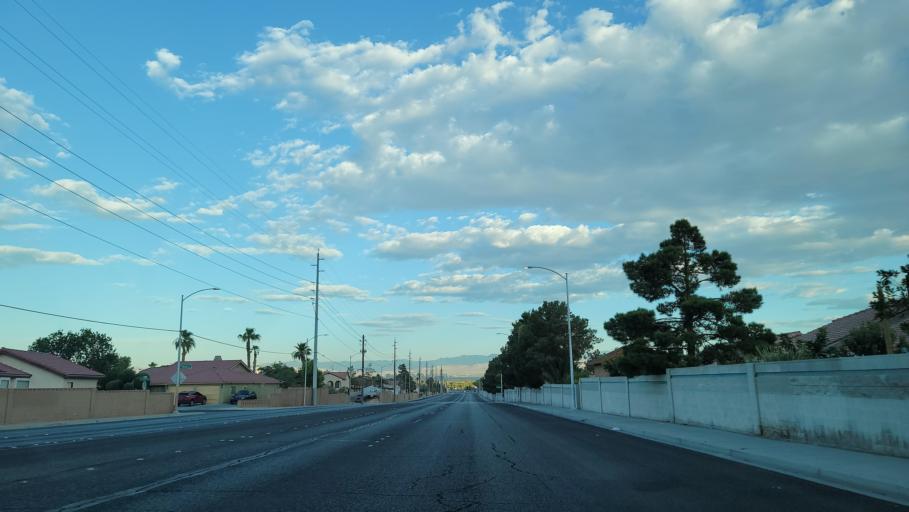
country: US
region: Nevada
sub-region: Clark County
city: Sunrise Manor
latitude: 36.1743
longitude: -115.0356
